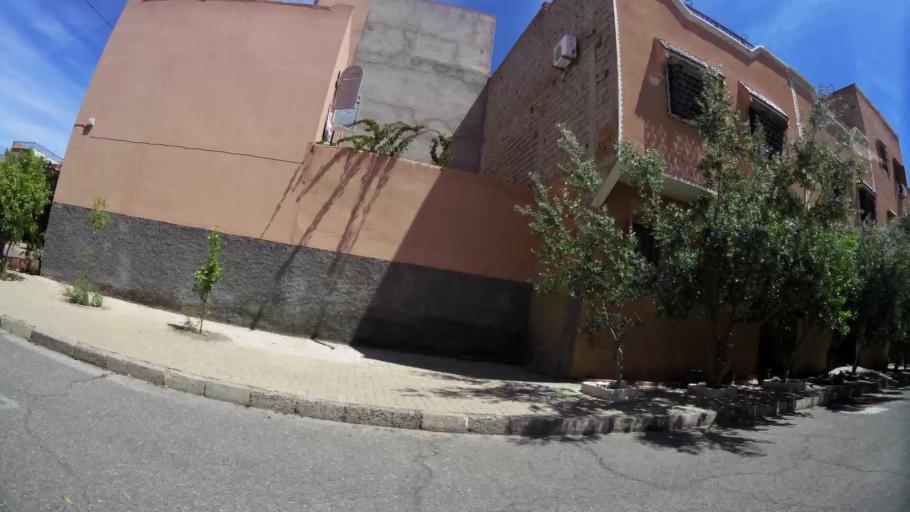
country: MA
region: Marrakech-Tensift-Al Haouz
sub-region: Marrakech
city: Marrakesh
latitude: 31.6413
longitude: -8.0535
